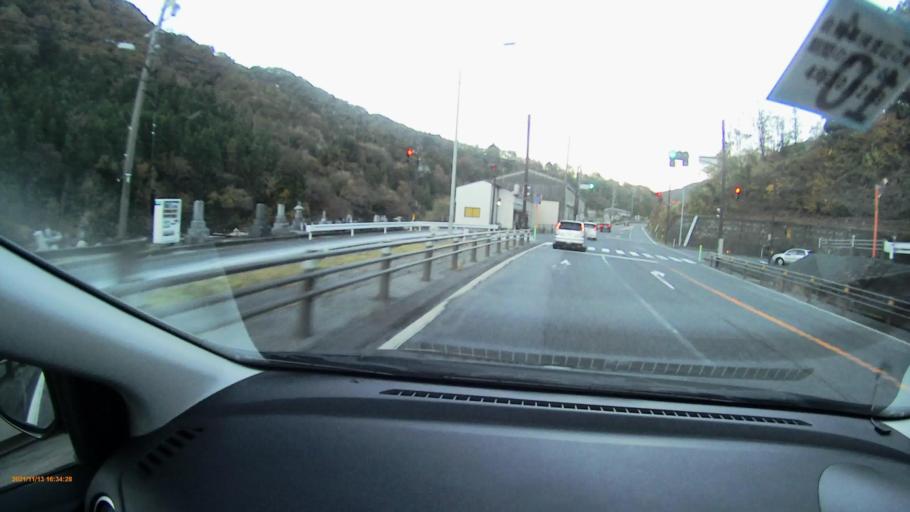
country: JP
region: Gifu
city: Nakatsugawa
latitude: 35.5932
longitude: 137.5986
